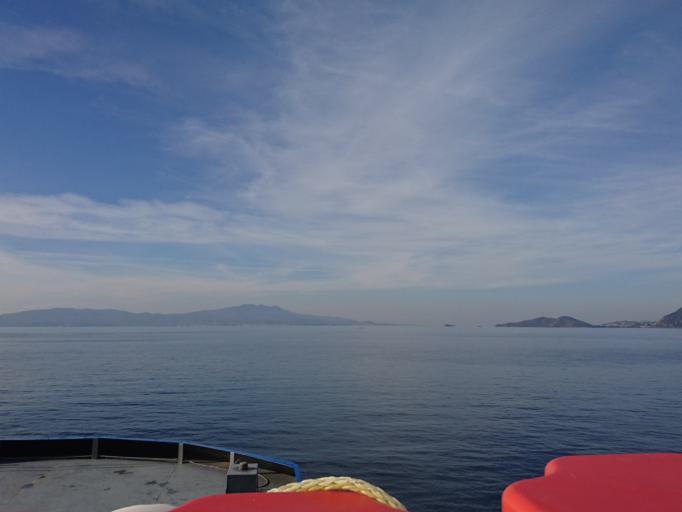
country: TR
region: Mugla
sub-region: Bodrum
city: Bodrum
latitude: 36.9896
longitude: 27.3916
